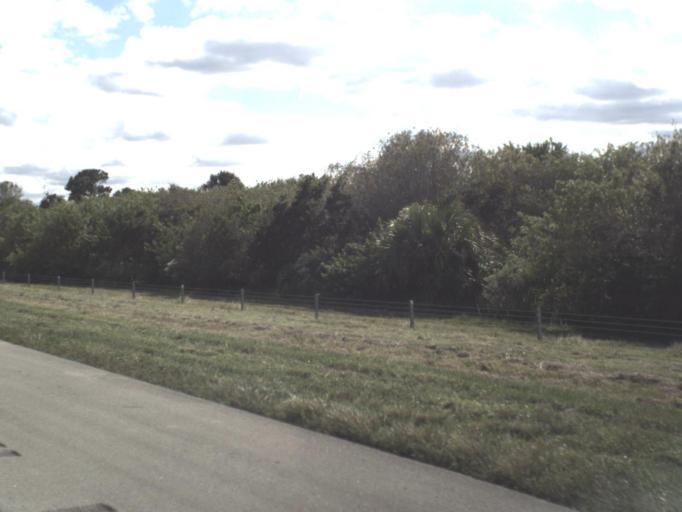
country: US
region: Florida
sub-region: Saint Lucie County
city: Lakewood Park
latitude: 27.4467
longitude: -80.4272
